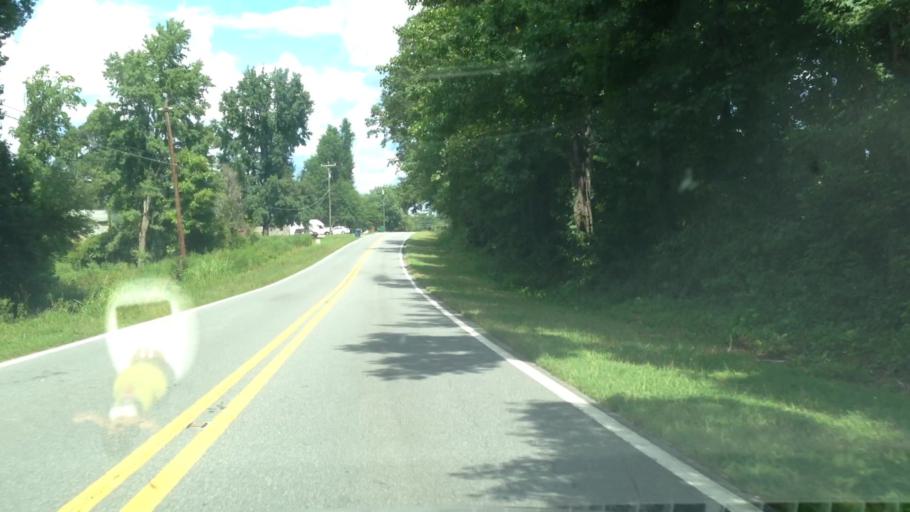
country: US
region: North Carolina
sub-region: Rockingham County
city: Reidsville
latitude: 36.3917
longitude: -79.6422
